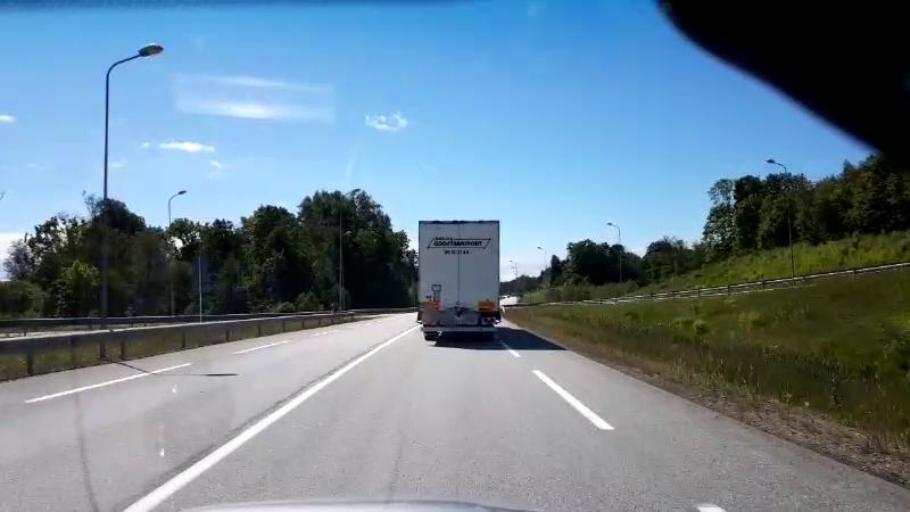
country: LV
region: Saulkrastu
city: Saulkrasti
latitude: 57.3262
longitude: 24.4550
